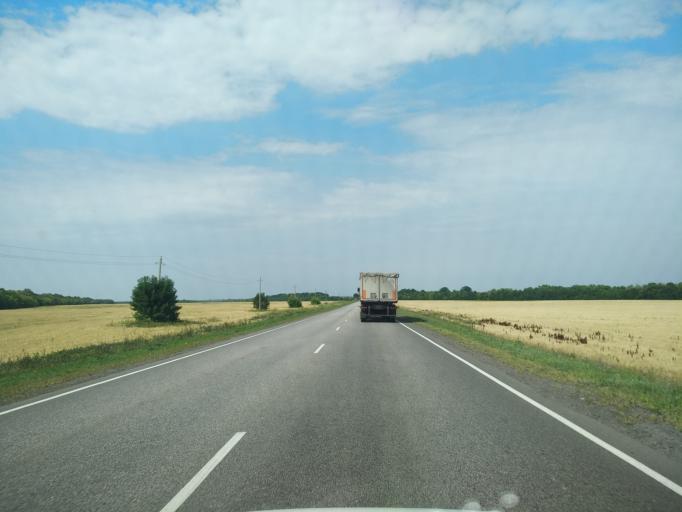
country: RU
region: Voronezj
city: Orlovo
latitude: 51.6774
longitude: 39.7788
